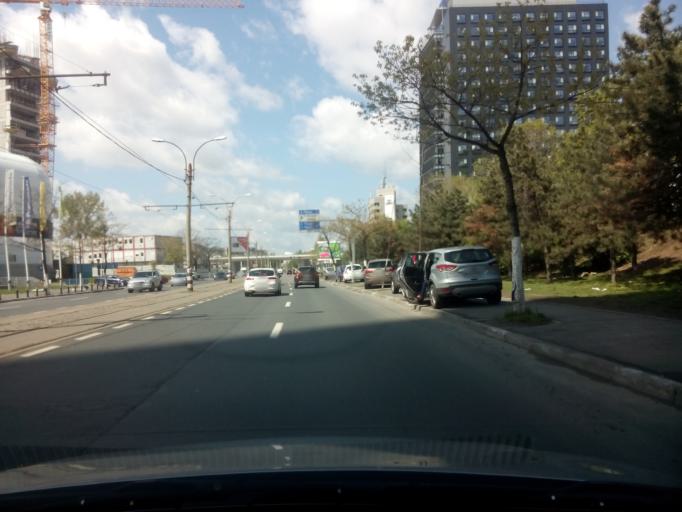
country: RO
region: Bucuresti
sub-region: Municipiul Bucuresti
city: Bucharest
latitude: 44.4786
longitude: 26.1048
